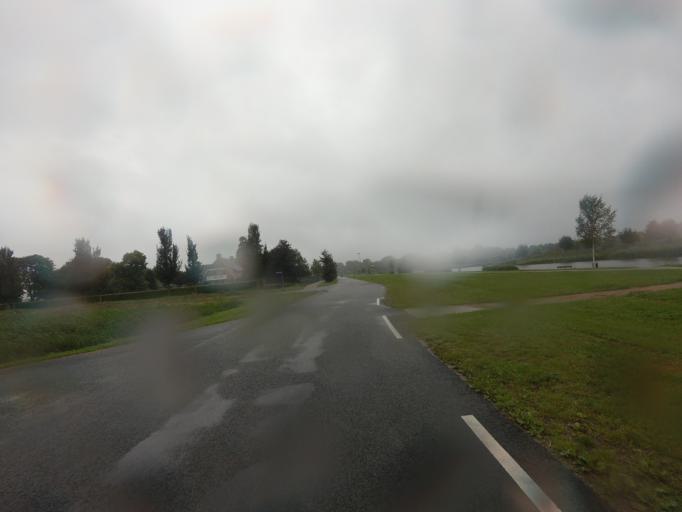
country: NL
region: North Holland
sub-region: Gemeente Huizen
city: Huizen
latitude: 52.3305
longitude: 5.2662
